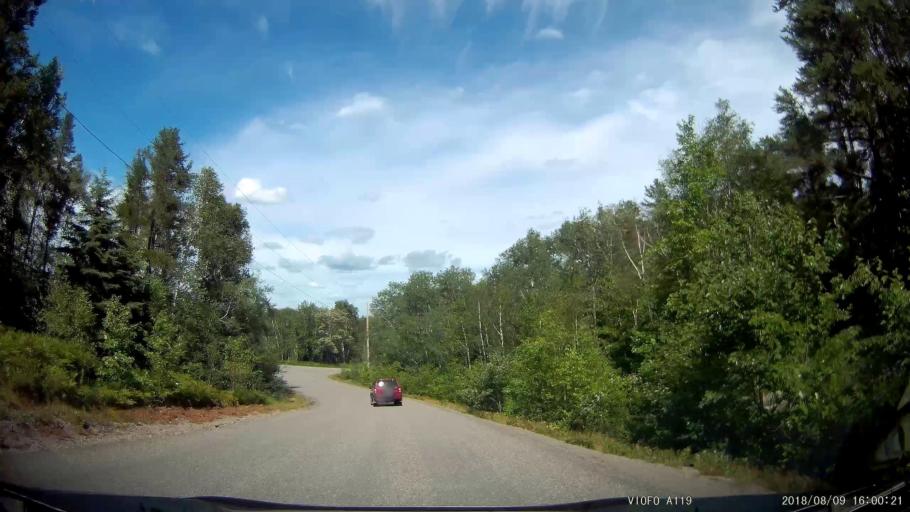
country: CA
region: Ontario
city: Rayside-Balfour
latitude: 46.6055
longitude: -81.4781
